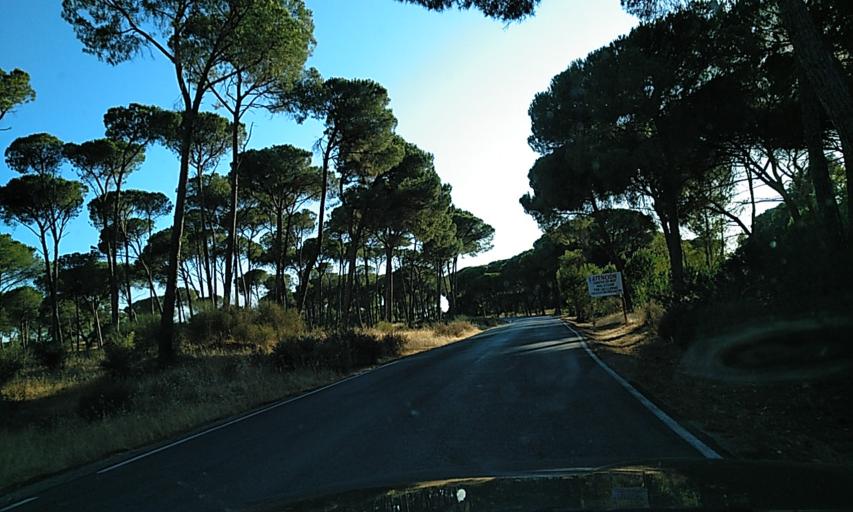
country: ES
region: Andalusia
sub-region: Provincia de Huelva
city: San Bartolome de la Torre
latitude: 37.3973
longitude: -7.1273
